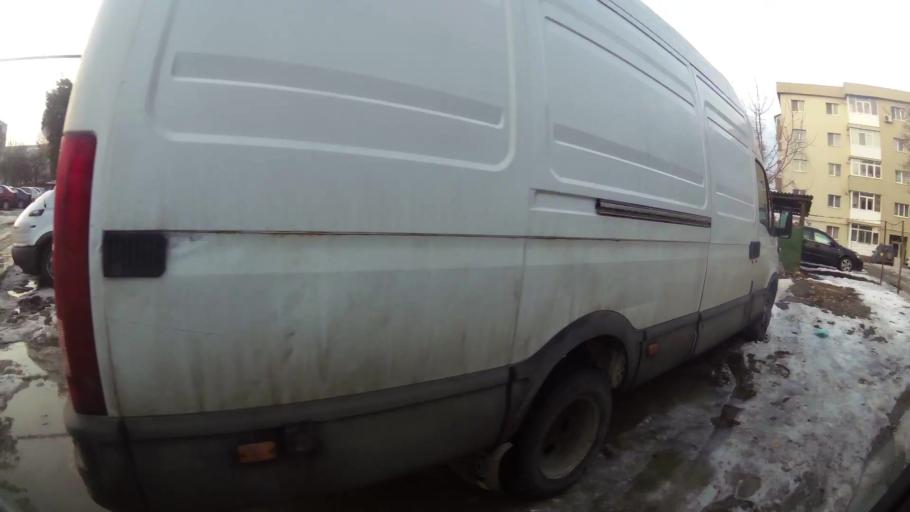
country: RO
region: Ilfov
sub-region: Comuna Popesti-Leordeni
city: Popesti-Leordeni
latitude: 44.3639
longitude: 26.1970
